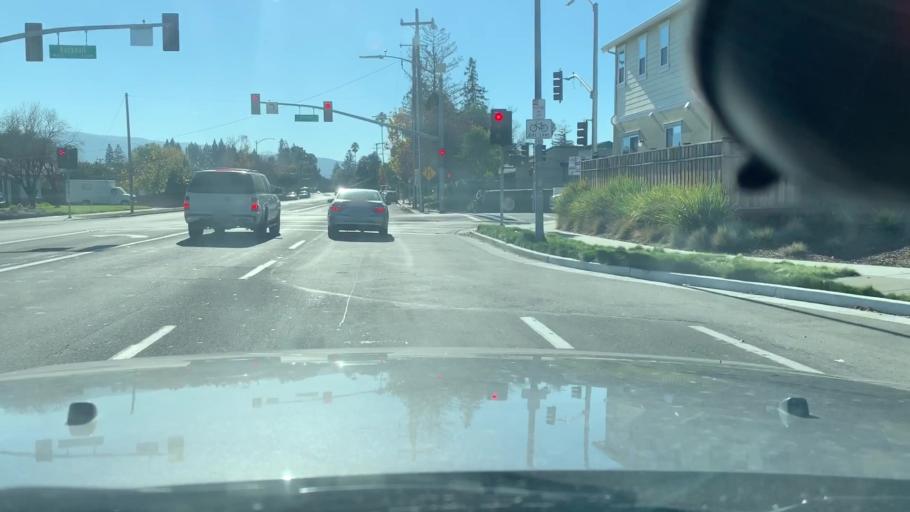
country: US
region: California
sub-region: Santa Clara County
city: Campbell
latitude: 37.2840
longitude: -121.9767
